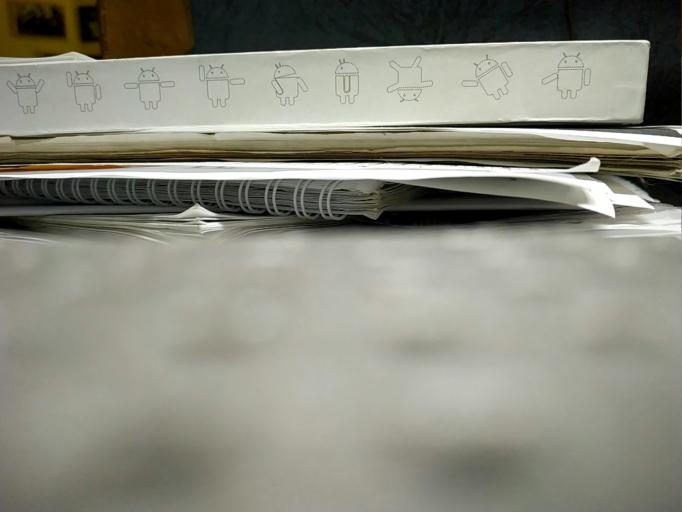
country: EE
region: Ida-Virumaa
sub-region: Narva-Joesuu linn
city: Narva-Joesuu
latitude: 59.7058
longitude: 27.8755
